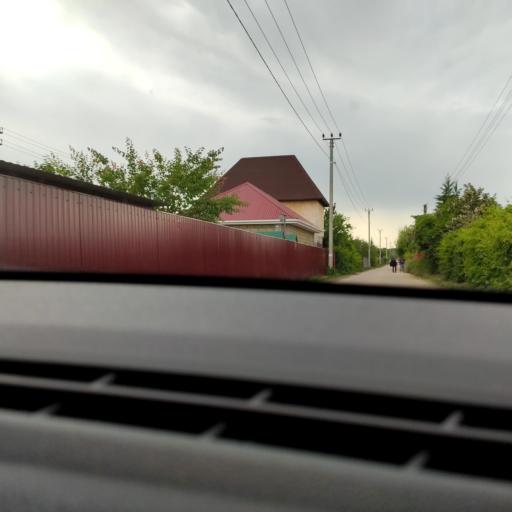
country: RU
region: Samara
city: Podstepki
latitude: 53.5116
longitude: 49.0750
